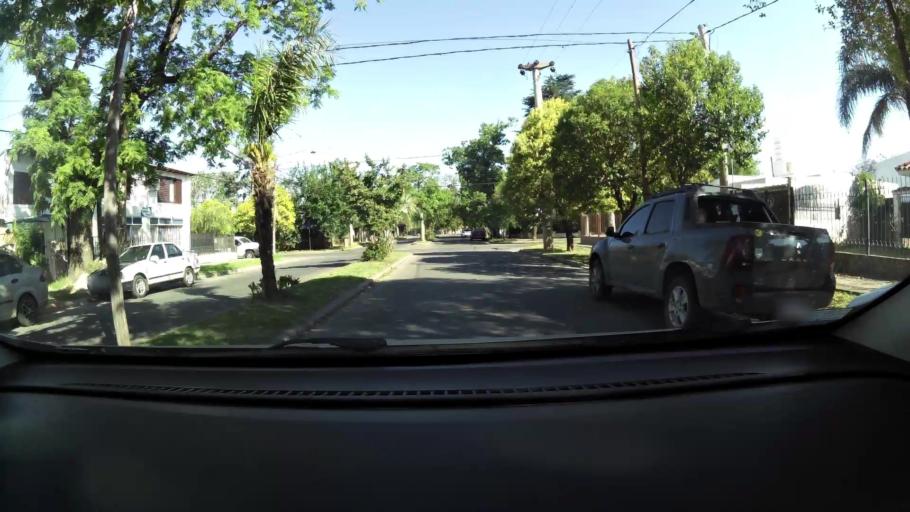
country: AR
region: Cordoba
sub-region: Departamento de Capital
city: Cordoba
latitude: -31.3616
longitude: -64.1992
